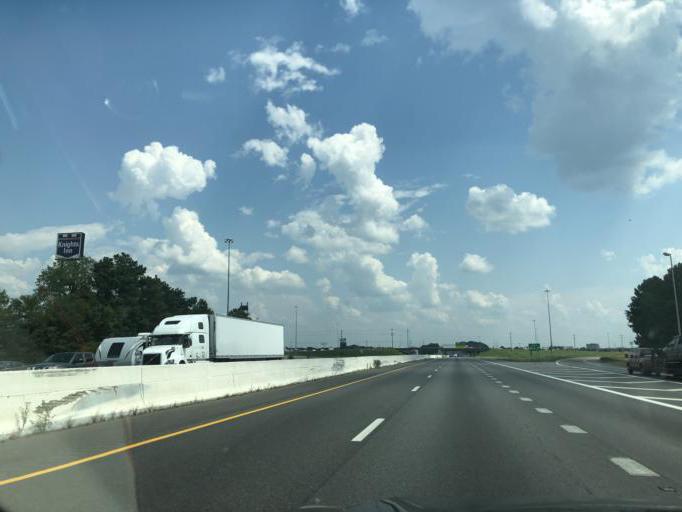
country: US
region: Tennessee
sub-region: Rutherford County
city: Murfreesboro
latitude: 35.8154
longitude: -86.4003
